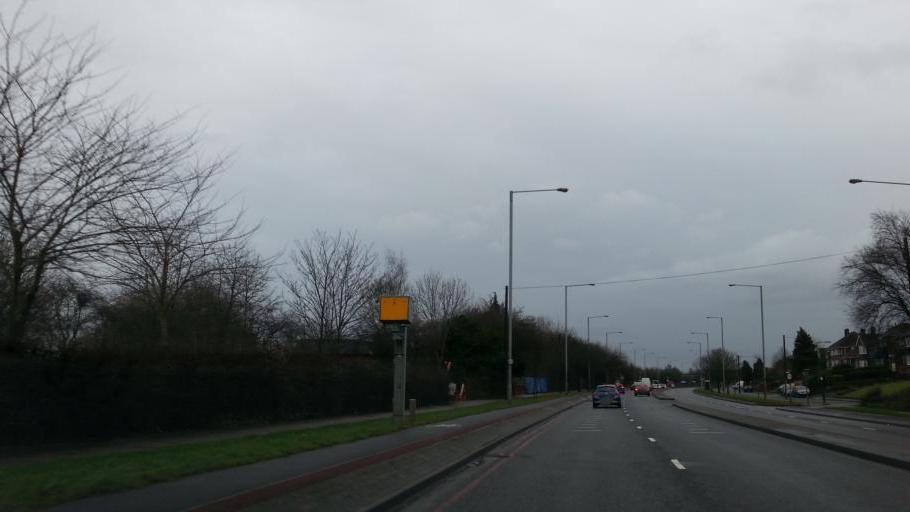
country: GB
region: England
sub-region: Sandwell
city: Tipton
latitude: 52.5113
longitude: -2.0499
